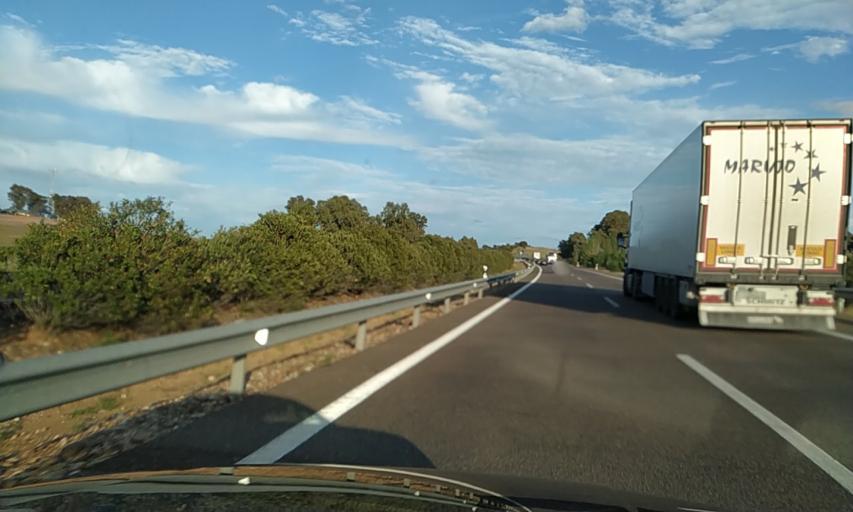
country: ES
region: Extremadura
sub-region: Provincia de Badajoz
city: Badajoz
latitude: 38.8745
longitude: -6.8771
